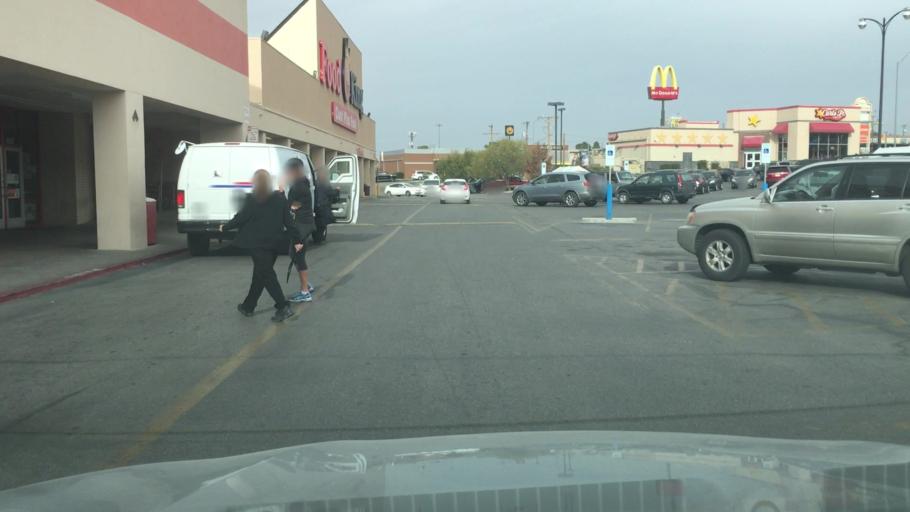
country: US
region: New Mexico
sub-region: Dona Ana County
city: Sunland Park
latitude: 31.8293
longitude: -106.5303
